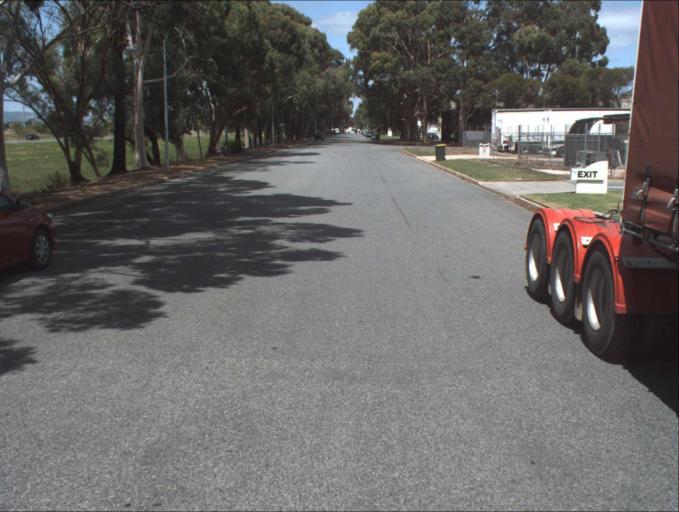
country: AU
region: South Australia
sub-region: Port Adelaide Enfield
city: Blair Athol
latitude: -34.8534
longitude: 138.5736
